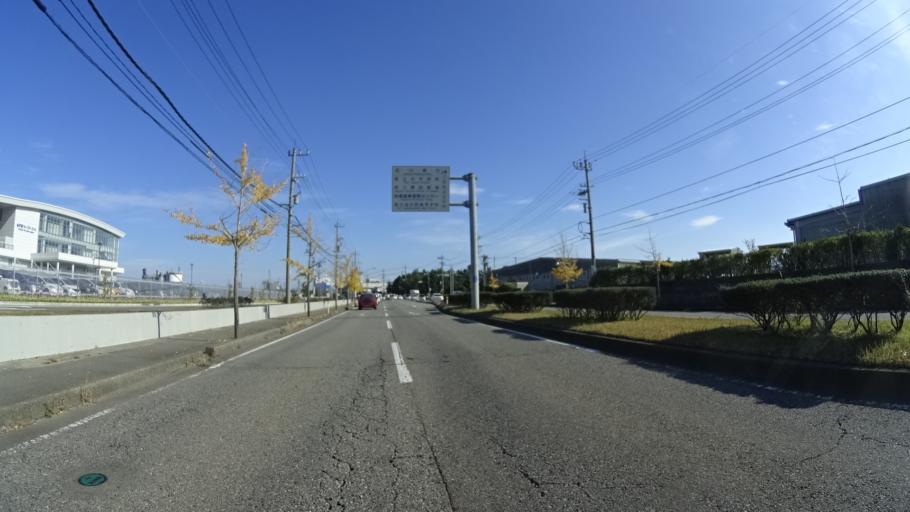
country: JP
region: Ishikawa
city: Kanazawa-shi
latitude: 36.6074
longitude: 136.6136
